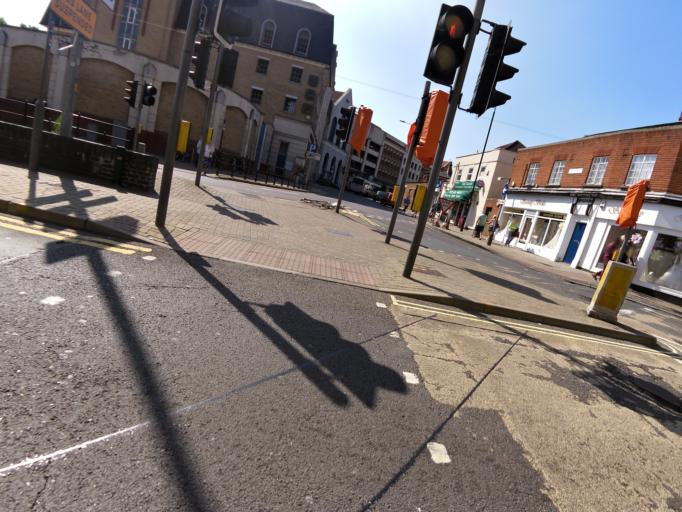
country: GB
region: England
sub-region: Essex
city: Colchester
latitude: 51.8868
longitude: 0.9035
